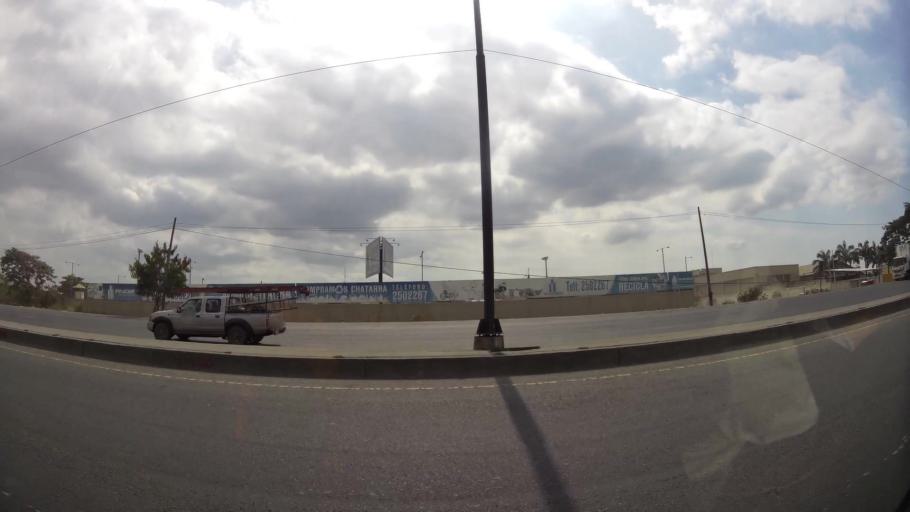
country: EC
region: Guayas
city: Santa Lucia
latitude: -2.0864
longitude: -79.9461
